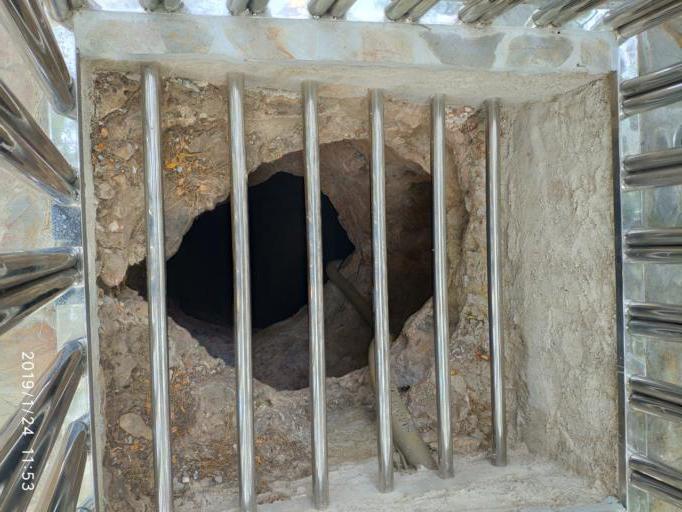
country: ES
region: Andalusia
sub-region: Provincia de Malaga
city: Nerja
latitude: 36.7621
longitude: -3.8452
